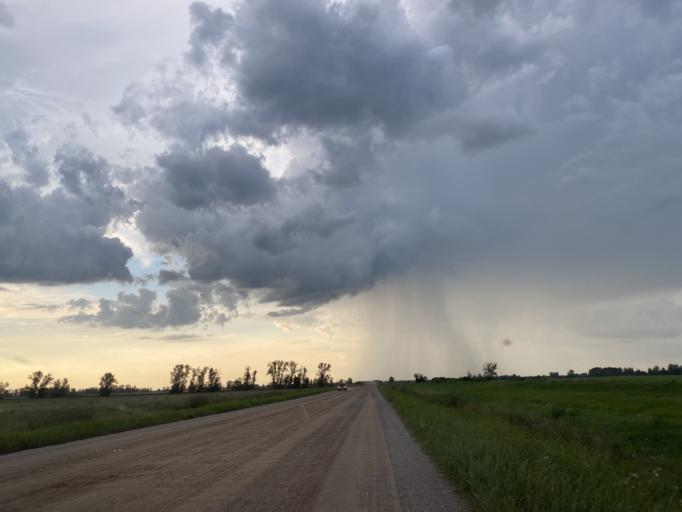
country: BY
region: Brest
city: Tsyelyakhany
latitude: 52.4585
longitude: 25.5714
